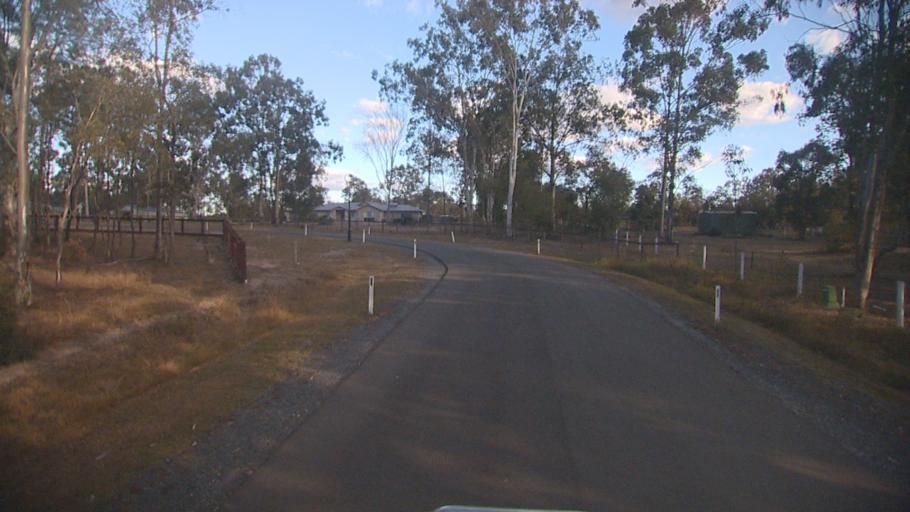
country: AU
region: Queensland
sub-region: Logan
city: Cedar Vale
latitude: -27.8583
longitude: 153.0923
